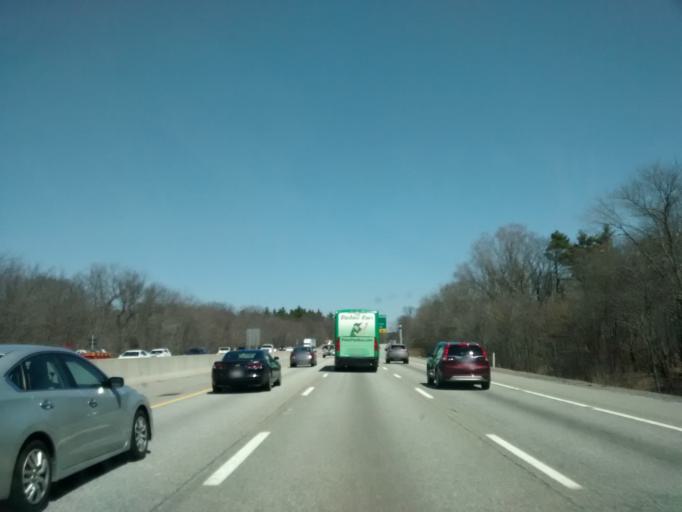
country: US
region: Massachusetts
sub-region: Worcester County
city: Westborough
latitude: 42.2582
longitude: -71.5785
